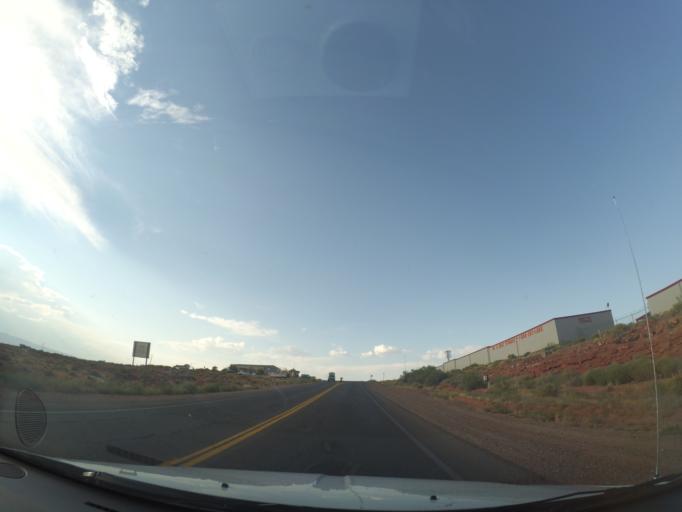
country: US
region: Arizona
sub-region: Coconino County
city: Page
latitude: 36.9057
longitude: -111.4547
